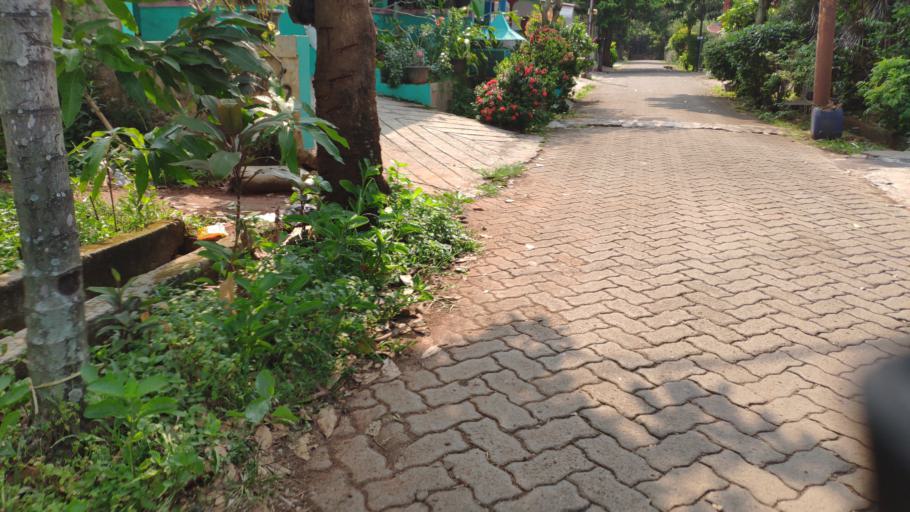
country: ID
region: West Java
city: Pamulang
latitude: -6.3140
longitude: 106.8102
